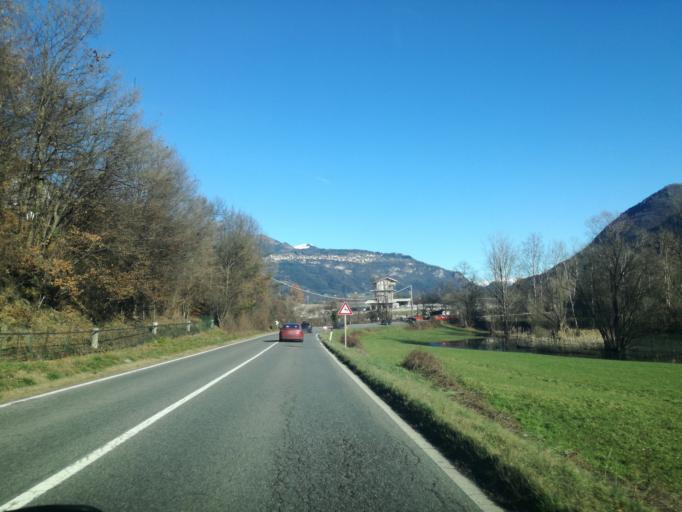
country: IT
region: Lombardy
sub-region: Provincia di Bergamo
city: Piangaiano
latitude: 45.7929
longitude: 10.0047
